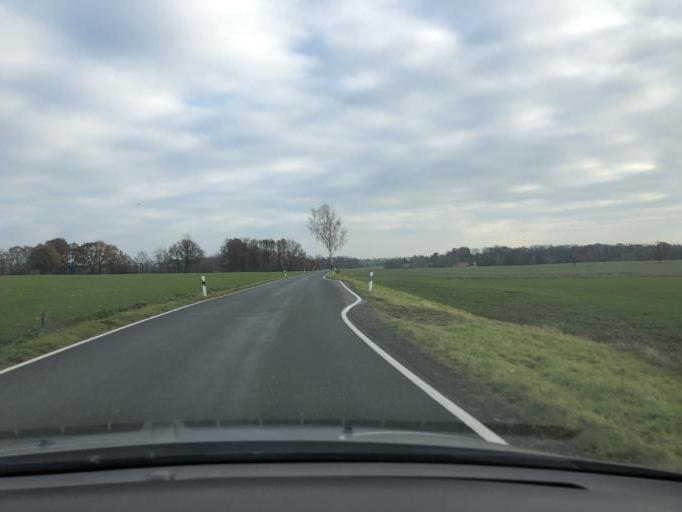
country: DE
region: Saxony
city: Mutzschen
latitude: 51.2835
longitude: 12.8666
